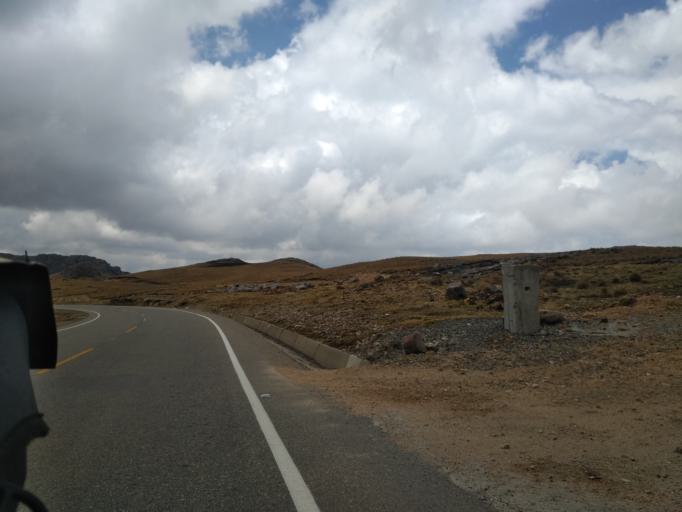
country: PE
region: La Libertad
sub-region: Provincia de Santiago de Chuco
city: Quiruvilca
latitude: -7.9679
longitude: -78.2036
